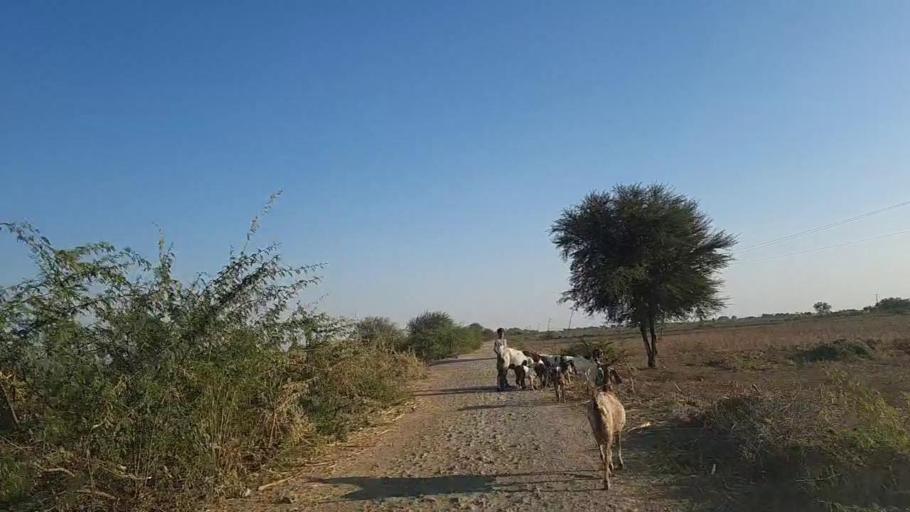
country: PK
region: Sindh
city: Naukot
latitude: 24.9862
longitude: 69.3856
